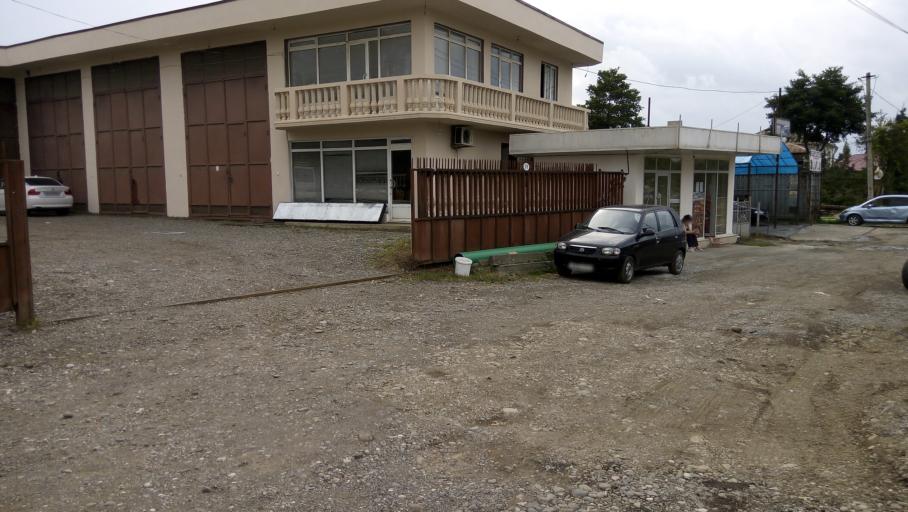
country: GE
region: Ajaria
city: Batumi
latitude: 41.6460
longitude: 41.6693
